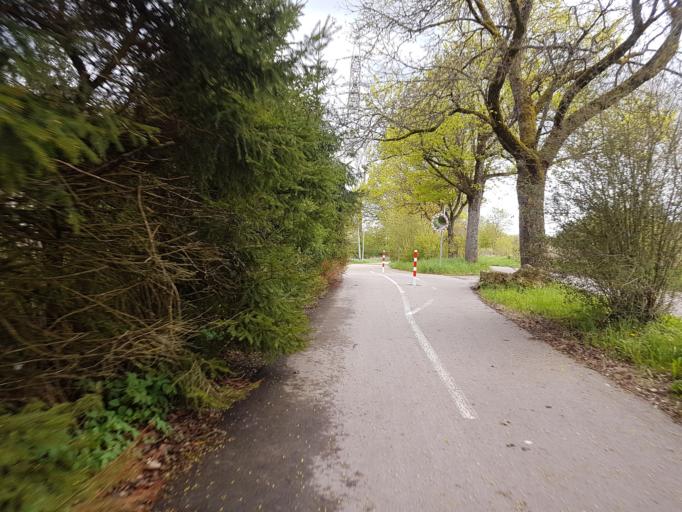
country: DE
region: Baden-Wuerttemberg
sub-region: Freiburg Region
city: Bad Durrheim
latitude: 48.0491
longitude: 8.5279
